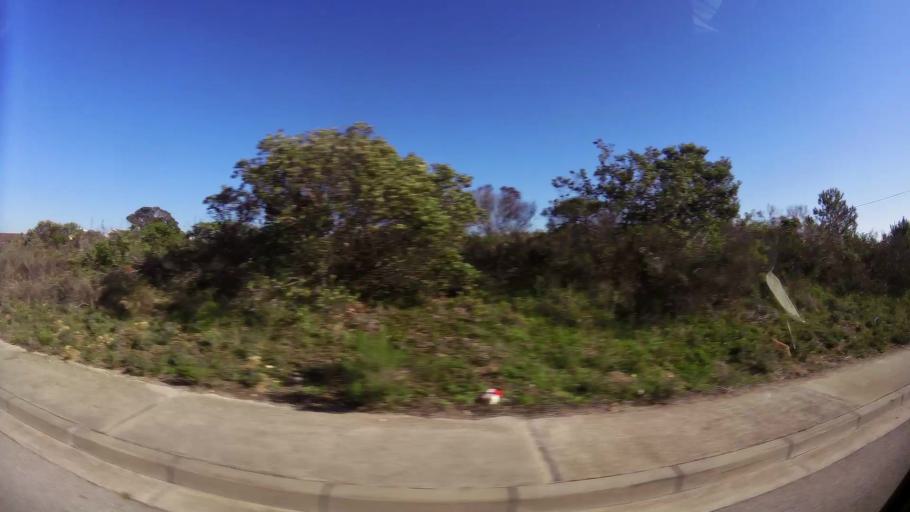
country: ZA
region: Eastern Cape
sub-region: Nelson Mandela Bay Metropolitan Municipality
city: Port Elizabeth
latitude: -33.9778
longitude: 25.6350
